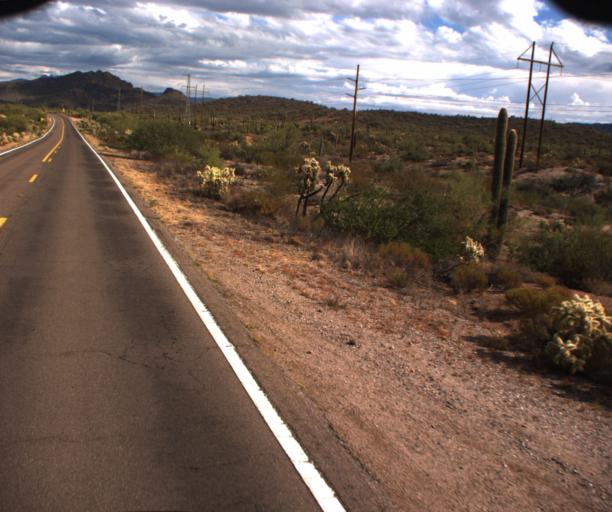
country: US
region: Arizona
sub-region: Pinal County
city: Apache Junction
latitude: 33.4832
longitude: -111.4708
